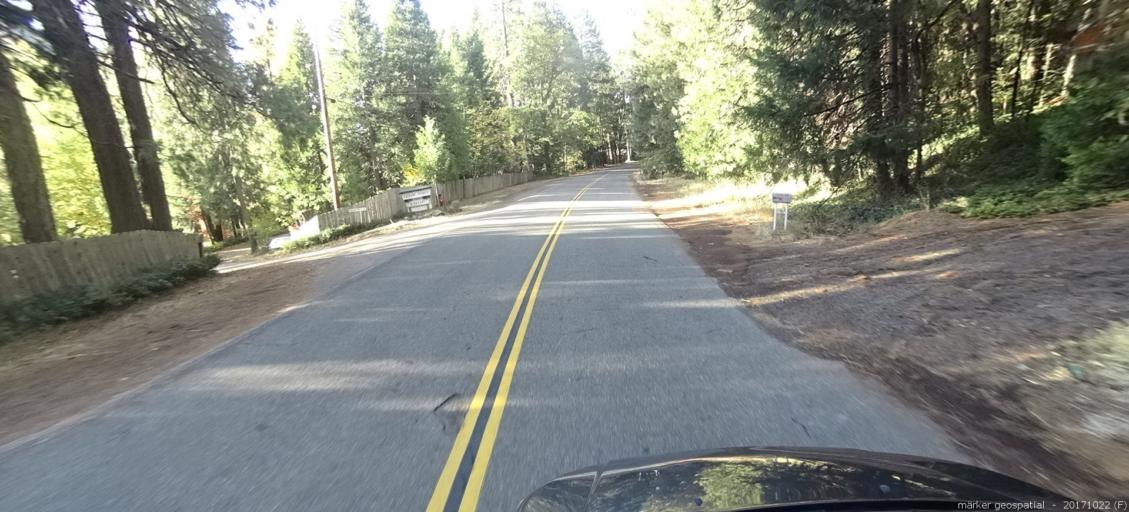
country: US
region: California
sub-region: Siskiyou County
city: Dunsmuir
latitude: 41.1774
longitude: -122.2917
